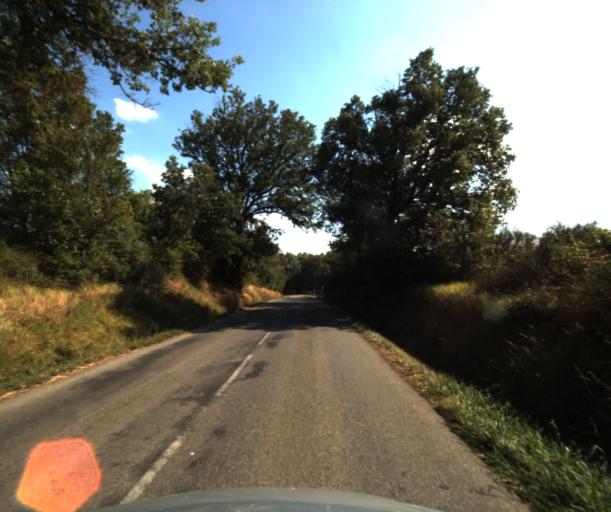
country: FR
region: Midi-Pyrenees
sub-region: Departement de la Haute-Garonne
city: Saint-Lys
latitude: 43.5183
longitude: 1.1797
